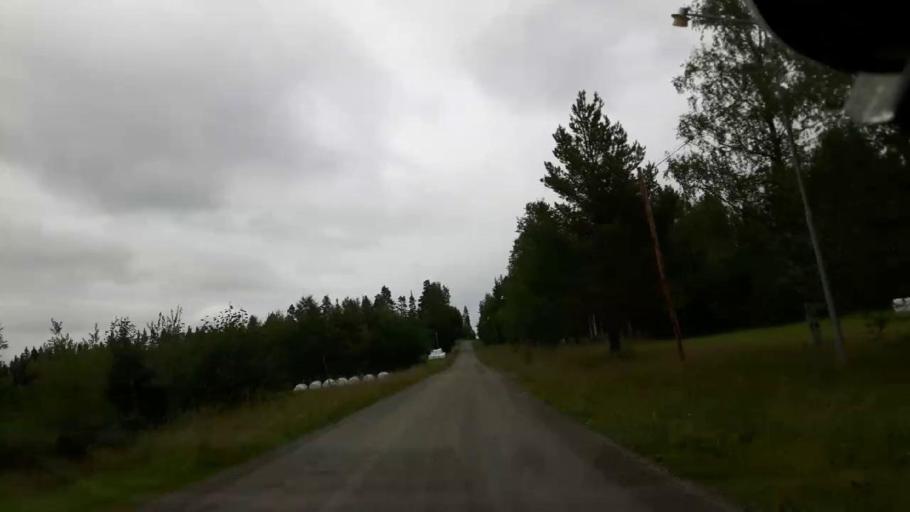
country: SE
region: Jaemtland
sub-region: Bergs Kommun
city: Hoverberg
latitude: 62.7959
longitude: 14.4634
